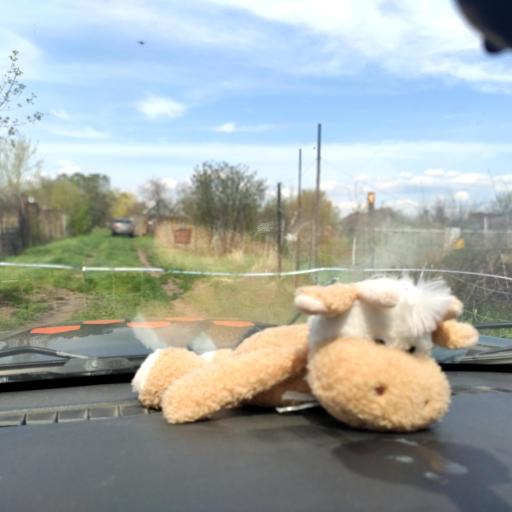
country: RU
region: Samara
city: Podstepki
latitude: 53.5114
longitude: 49.0854
